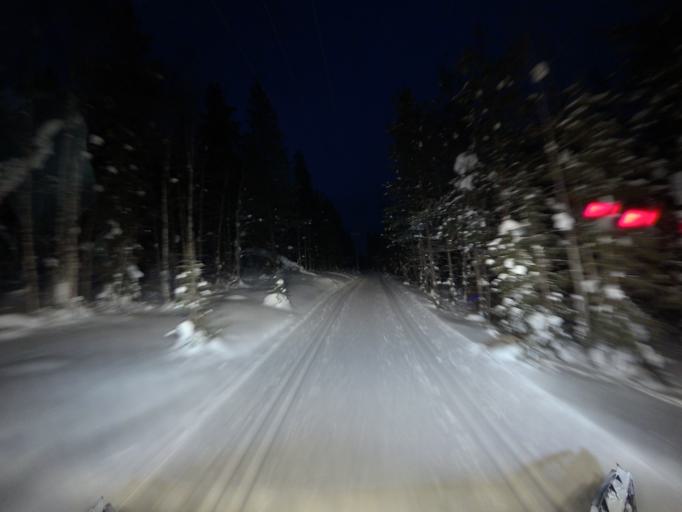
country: FI
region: Lapland
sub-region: Tunturi-Lappi
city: Kolari
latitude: 67.5846
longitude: 24.0836
